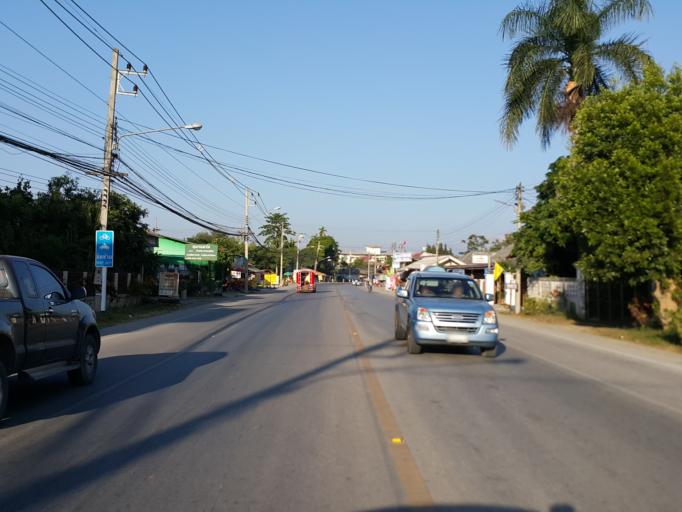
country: TH
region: Chiang Mai
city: San Kamphaeng
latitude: 18.7919
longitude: 99.1023
